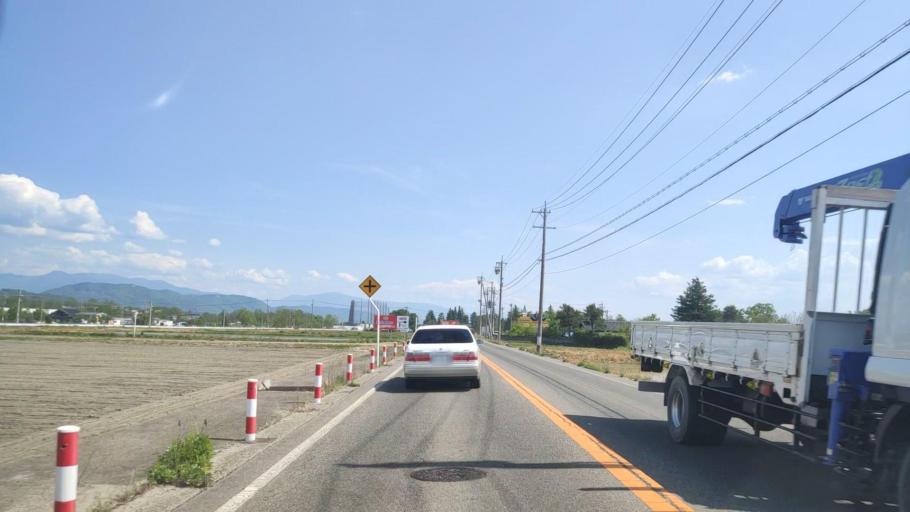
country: JP
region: Nagano
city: Hotaka
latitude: 36.3862
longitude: 137.8655
